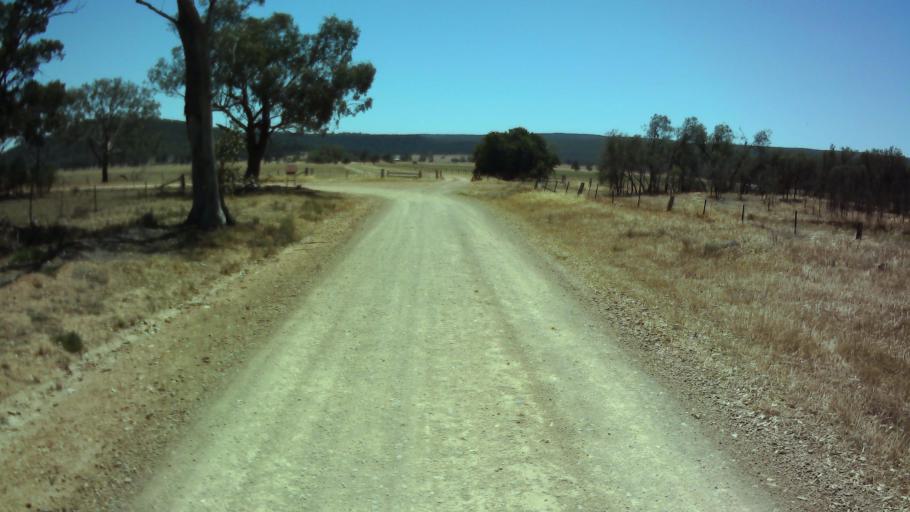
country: AU
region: New South Wales
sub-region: Weddin
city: Grenfell
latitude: -33.9934
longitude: 147.9582
